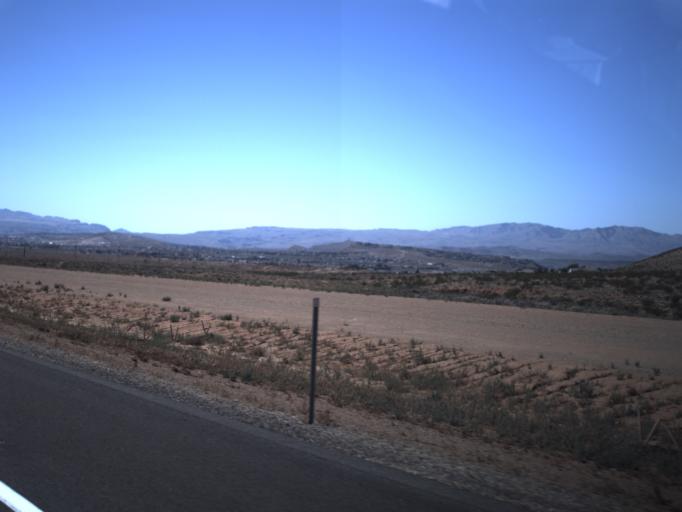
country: US
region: Utah
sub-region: Washington County
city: Washington
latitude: 37.0881
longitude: -113.4747
